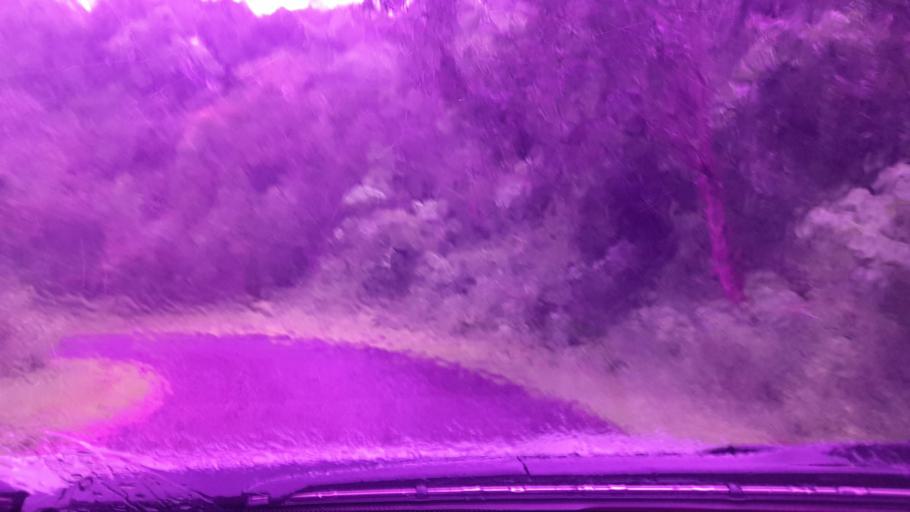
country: ET
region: Oromiya
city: Metu
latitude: 8.4725
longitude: 35.6390
